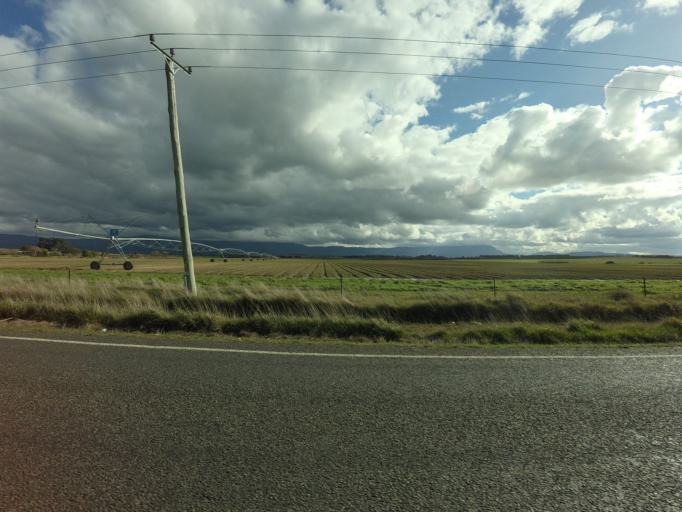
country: AU
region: Tasmania
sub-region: Northern Midlands
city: Longford
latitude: -41.7092
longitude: 147.0805
